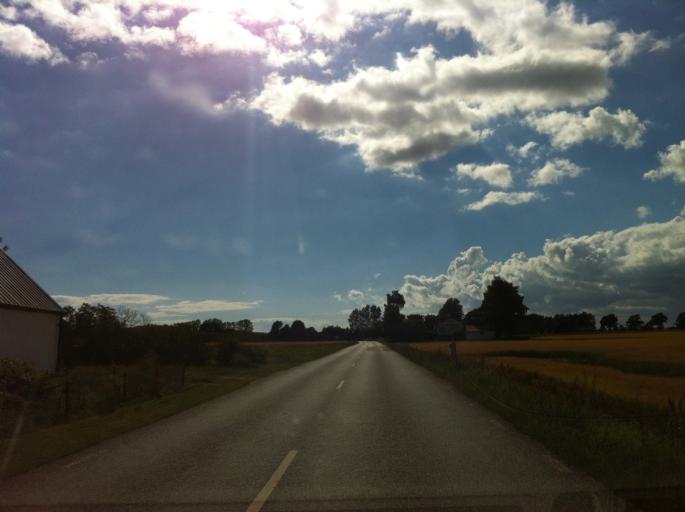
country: SE
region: Skane
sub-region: Ystads Kommun
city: Kopingebro
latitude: 55.3967
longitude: 14.0342
